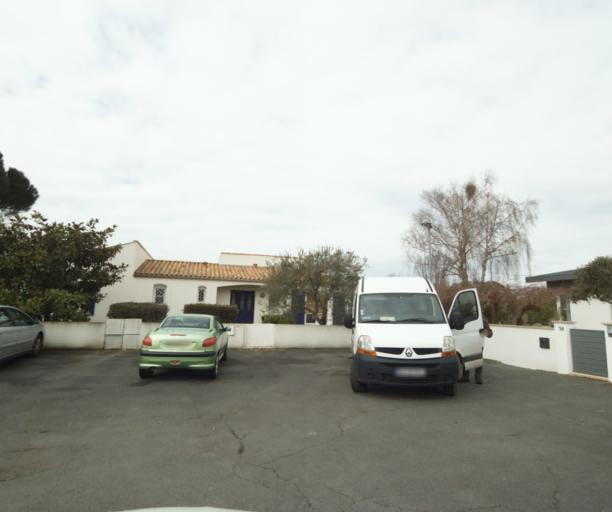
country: FR
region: Poitou-Charentes
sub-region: Departement de la Charente-Maritime
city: Lagord
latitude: 46.1890
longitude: -1.1675
